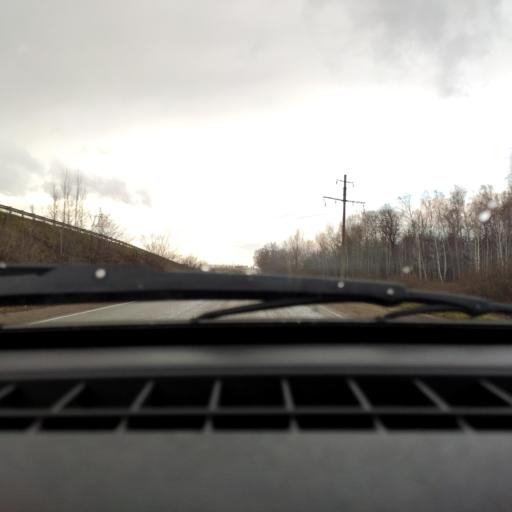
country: RU
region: Bashkortostan
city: Iglino
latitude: 54.7435
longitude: 56.3039
